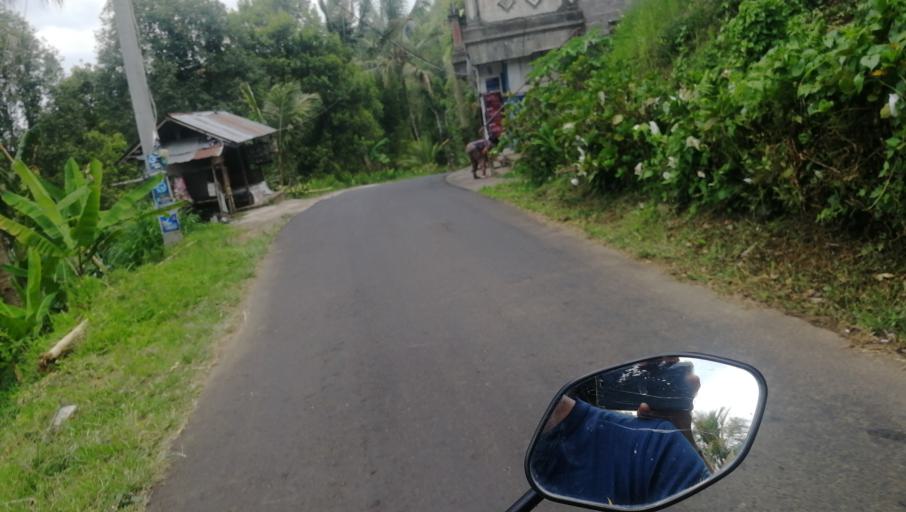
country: ID
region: Bali
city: Munduk
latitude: -8.2880
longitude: 115.0395
